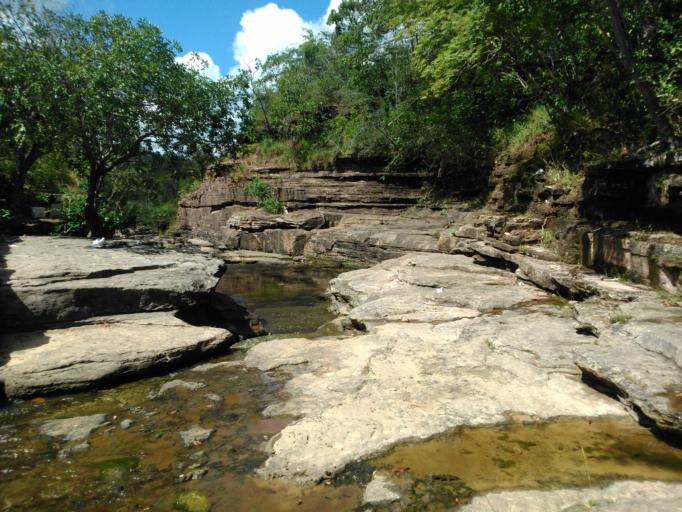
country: BR
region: Piaui
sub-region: Alto Longa
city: Alto Longa
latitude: -5.1956
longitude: -42.2596
